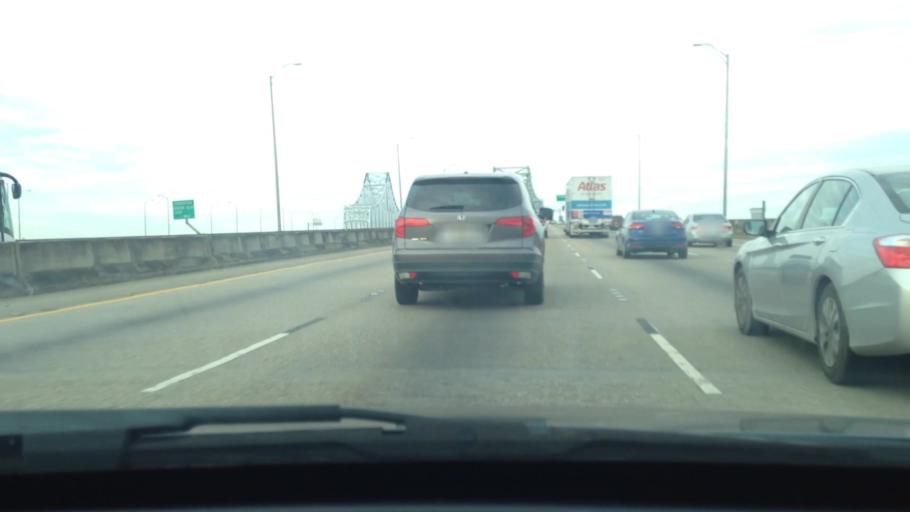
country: US
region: Louisiana
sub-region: Jefferson Parish
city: Gretna
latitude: 29.9386
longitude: -90.0451
